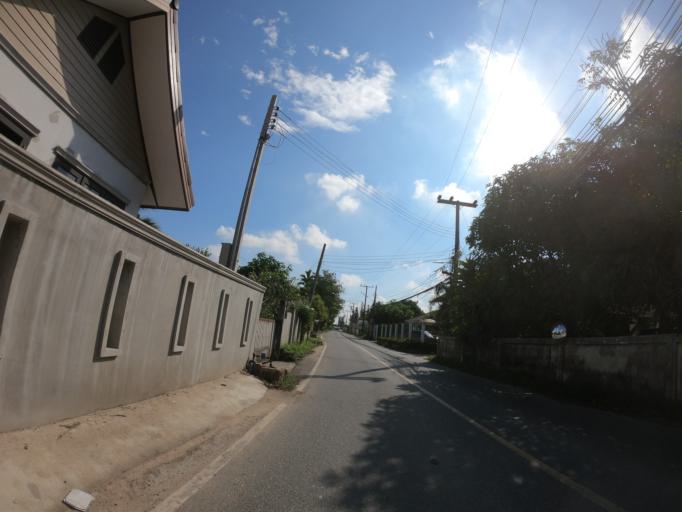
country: TH
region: Chiang Mai
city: San Sai
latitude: 18.8367
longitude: 99.0576
